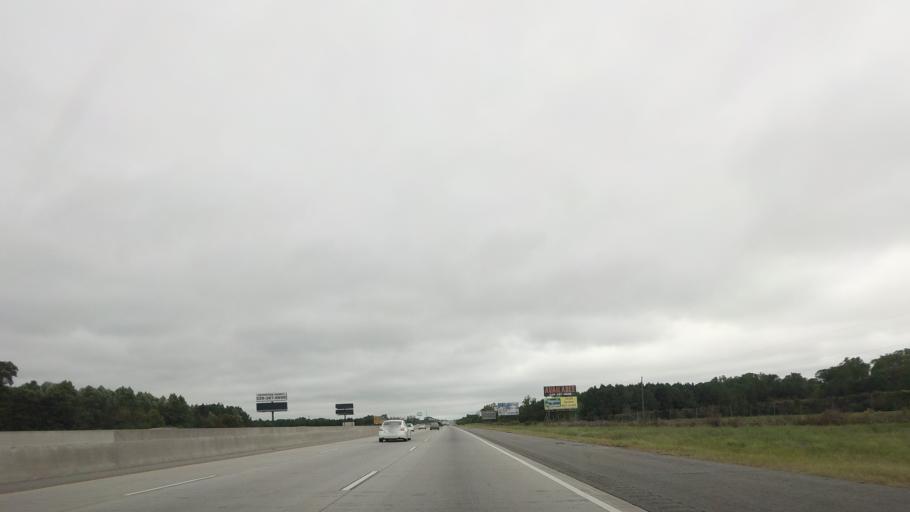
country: US
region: Georgia
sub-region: Tift County
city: Unionville
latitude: 31.3936
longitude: -83.4991
